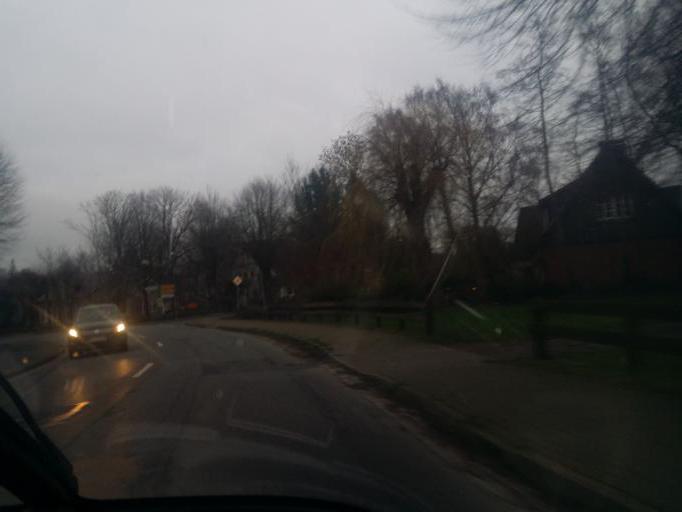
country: DE
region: Schleswig-Holstein
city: Hennstedt
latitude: 54.2834
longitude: 9.1616
